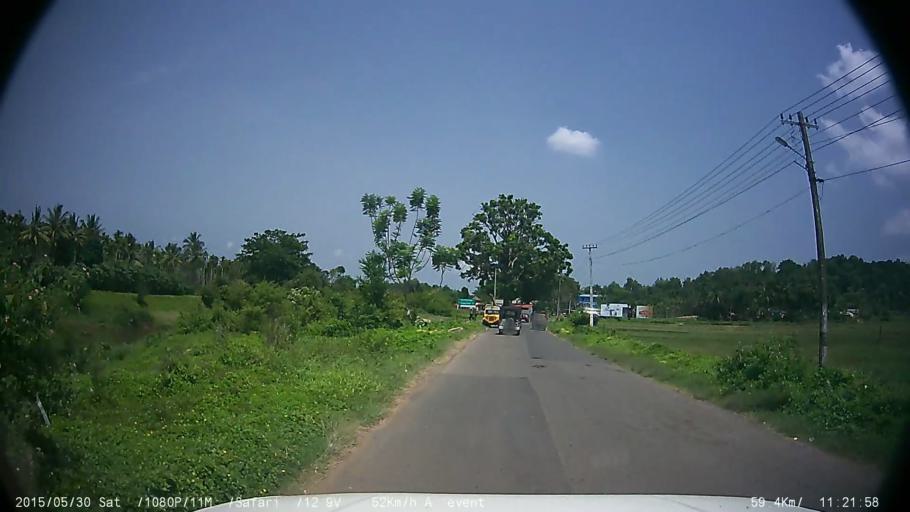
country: IN
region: Kerala
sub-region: Wayanad
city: Panamaram
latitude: 11.8024
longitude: 76.0337
